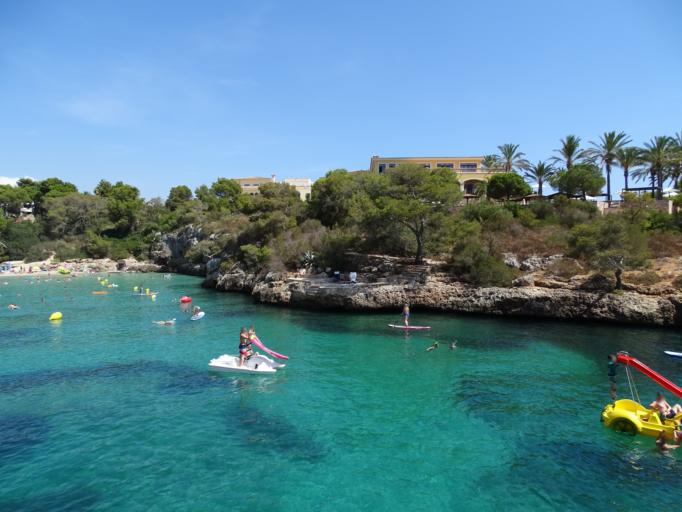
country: ES
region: Balearic Islands
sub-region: Illes Balears
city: Santanyi
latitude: 39.3785
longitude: 3.2398
